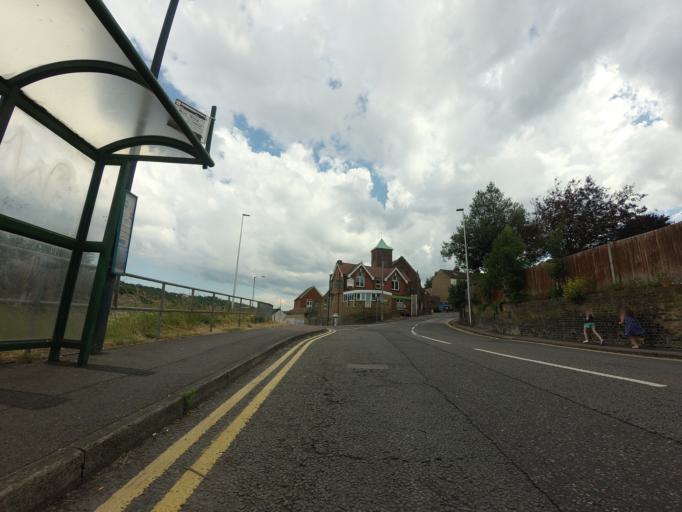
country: GB
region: England
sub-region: Kent
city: Chatham
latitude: 51.3757
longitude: 0.5348
